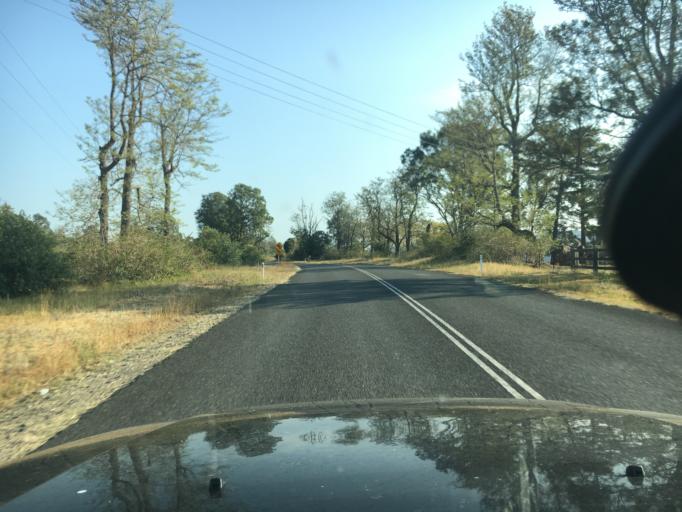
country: AU
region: New South Wales
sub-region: Cessnock
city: Branxton
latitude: -32.6227
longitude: 151.3601
